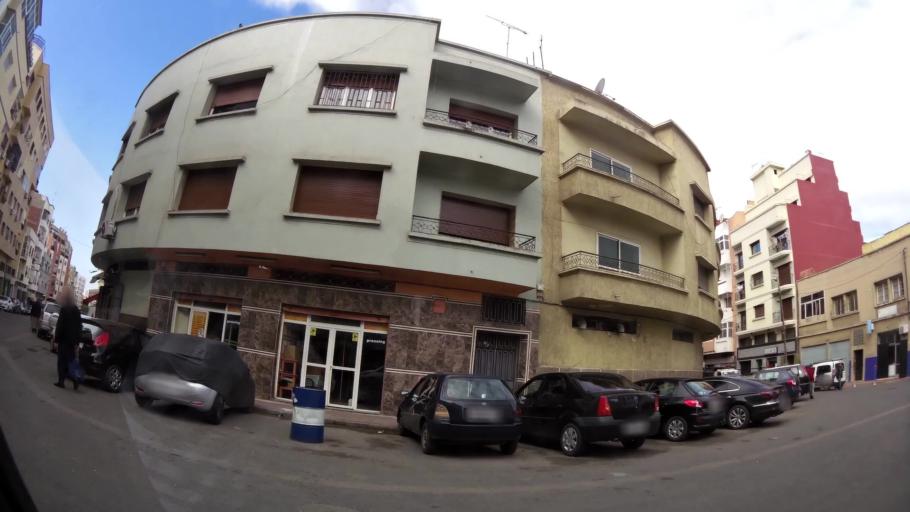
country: MA
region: Grand Casablanca
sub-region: Casablanca
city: Casablanca
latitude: 33.5946
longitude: -7.5902
